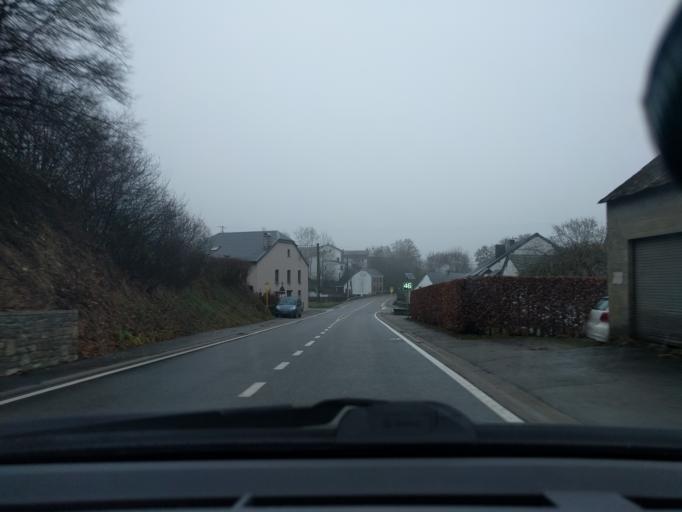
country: BE
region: Wallonia
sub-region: Province du Luxembourg
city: Gouvy
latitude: 50.1867
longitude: 5.9384
